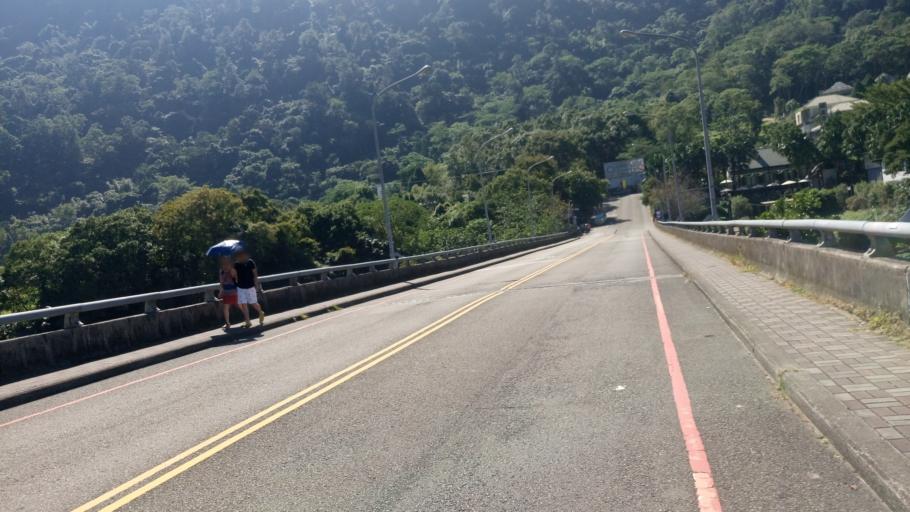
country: TW
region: Taiwan
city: Daxi
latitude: 24.7027
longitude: 121.1826
